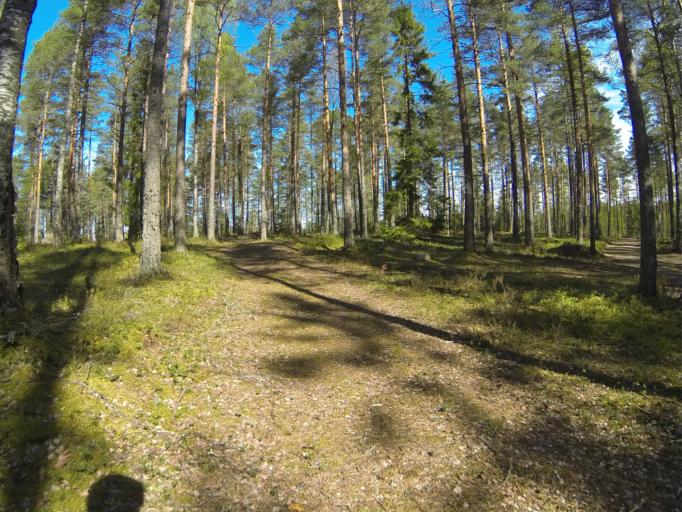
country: FI
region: Varsinais-Suomi
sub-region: Salo
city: Salo
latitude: 60.3964
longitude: 23.1976
